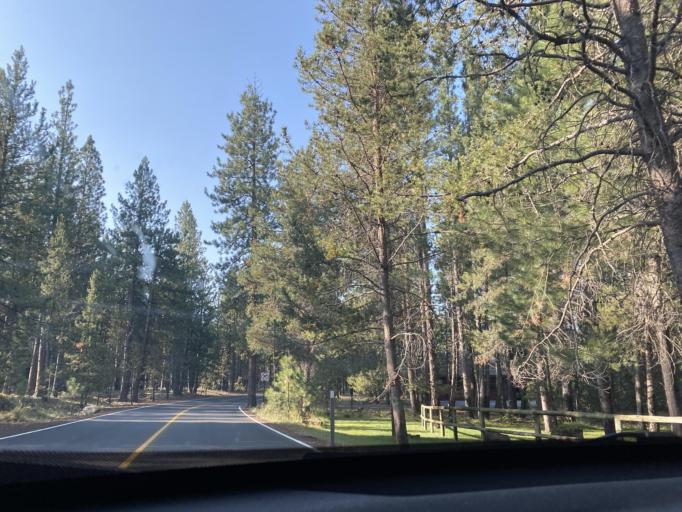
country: US
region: Oregon
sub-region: Deschutes County
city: Sunriver
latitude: 43.8886
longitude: -121.4384
